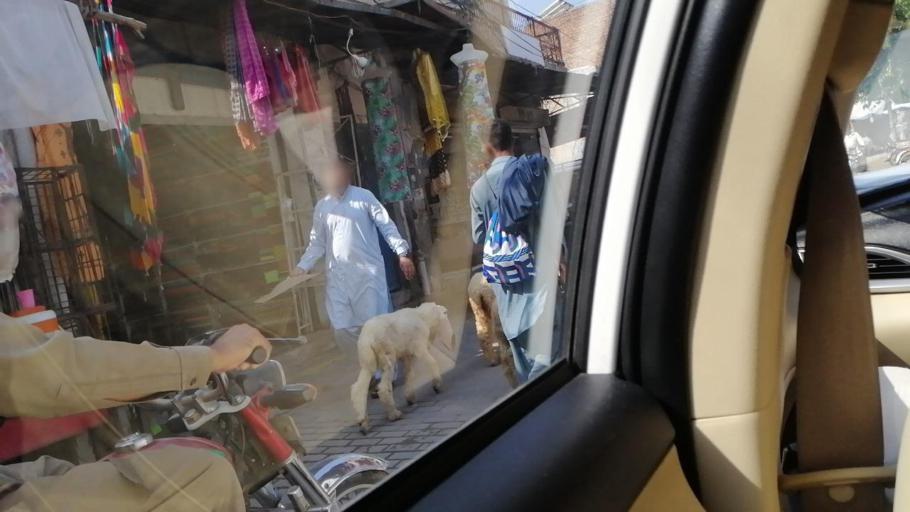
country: PK
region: Punjab
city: Kamalia
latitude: 30.7267
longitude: 72.6536
